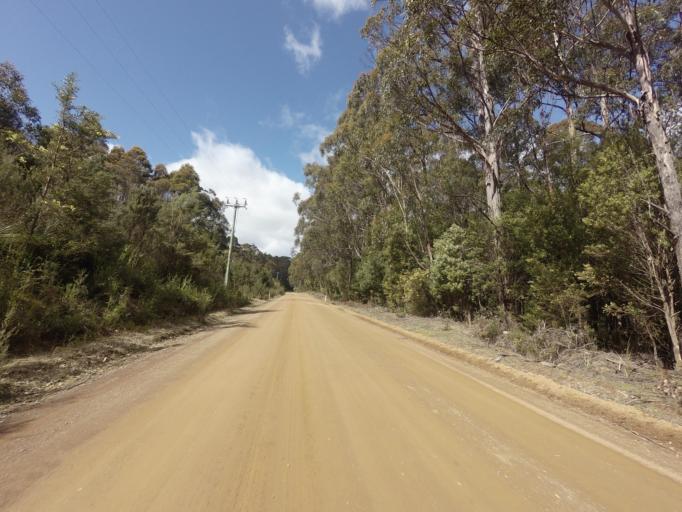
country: AU
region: Tasmania
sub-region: Huon Valley
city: Geeveston
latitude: -43.4137
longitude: 146.9041
